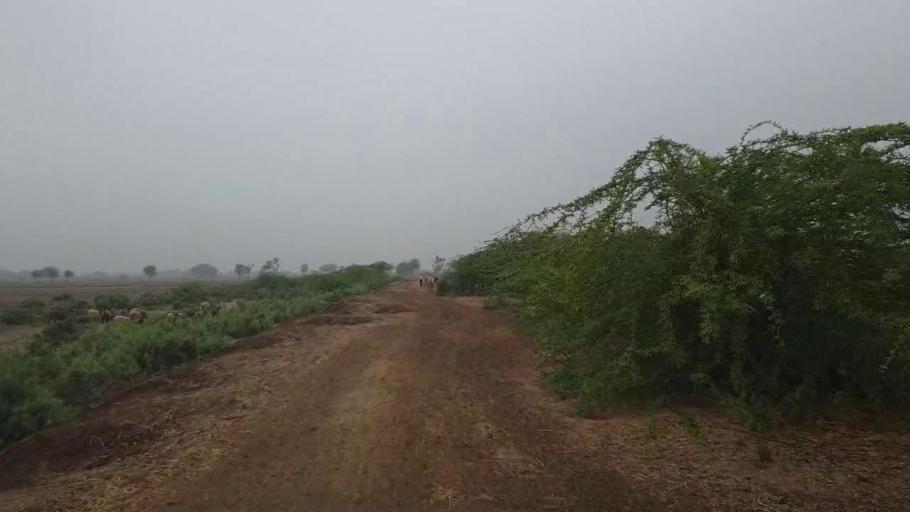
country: PK
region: Sindh
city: Badin
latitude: 24.6290
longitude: 68.6896
